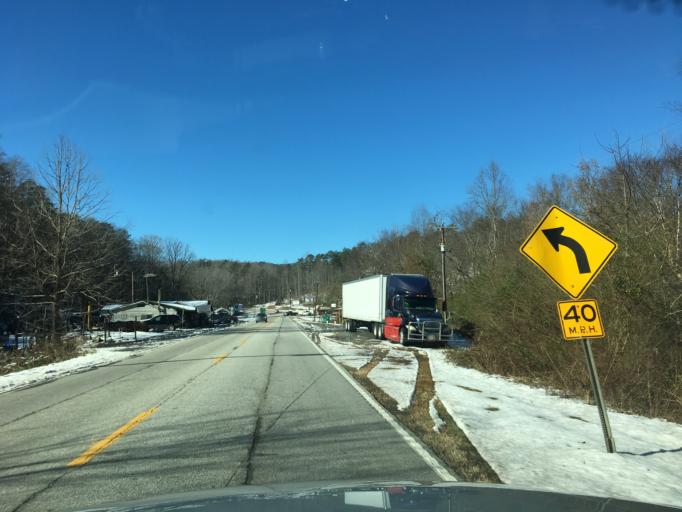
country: US
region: South Carolina
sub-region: Greenville County
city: Slater-Marietta
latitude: 35.0775
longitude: -82.5355
